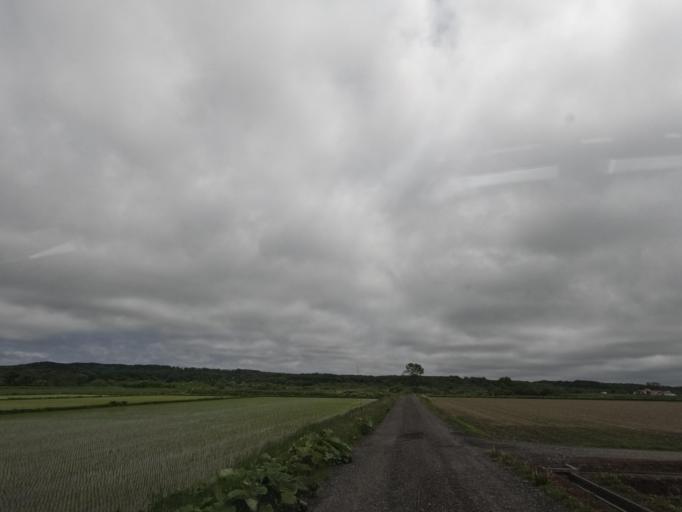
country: JP
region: Hokkaido
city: Tobetsu
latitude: 43.2474
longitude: 141.5200
